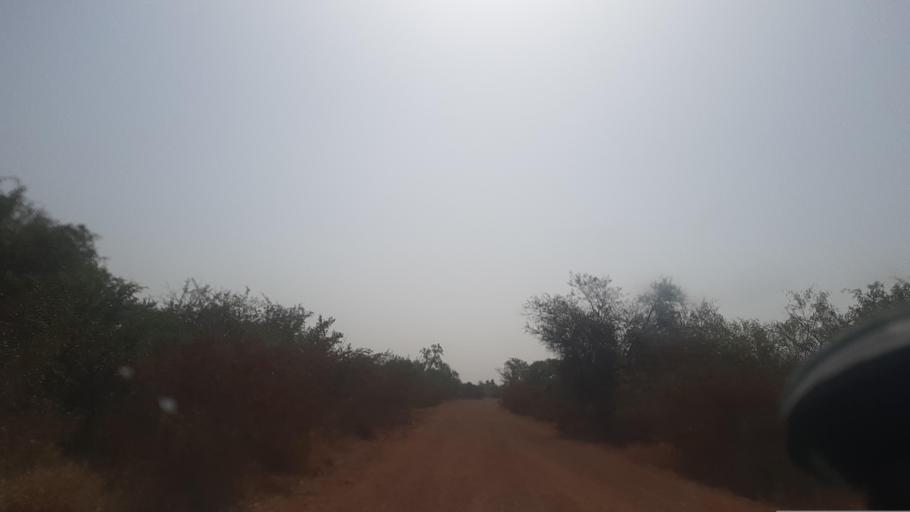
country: ML
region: Segou
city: Baroueli
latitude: 13.0675
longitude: -6.4786
